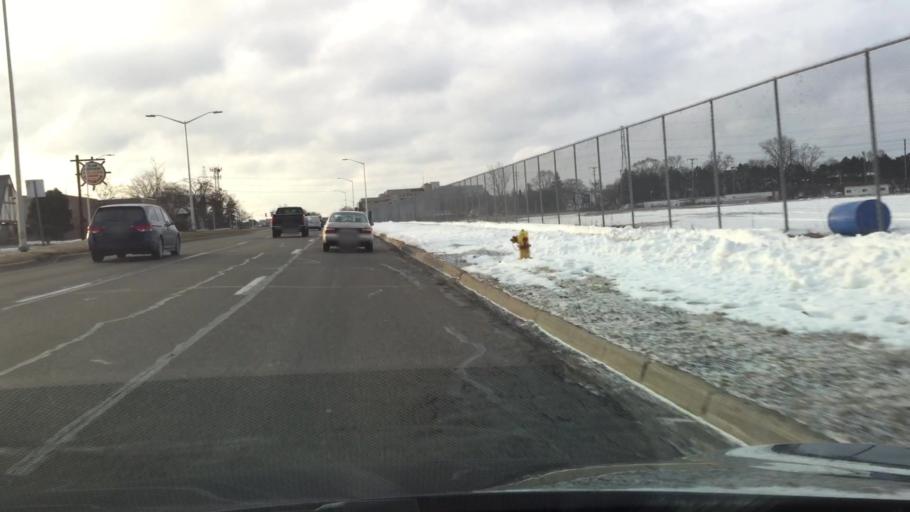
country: US
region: Michigan
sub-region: Oakland County
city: Pontiac
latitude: 42.6222
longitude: -83.2819
